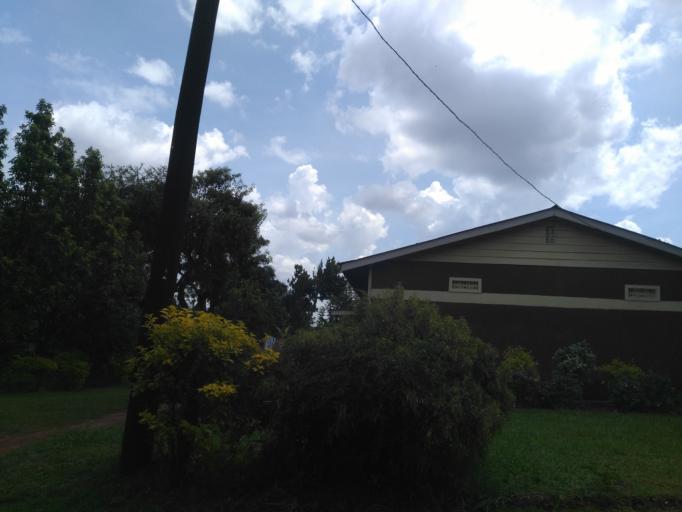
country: UG
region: Central Region
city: Kampala Central Division
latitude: 0.3610
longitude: 32.5838
